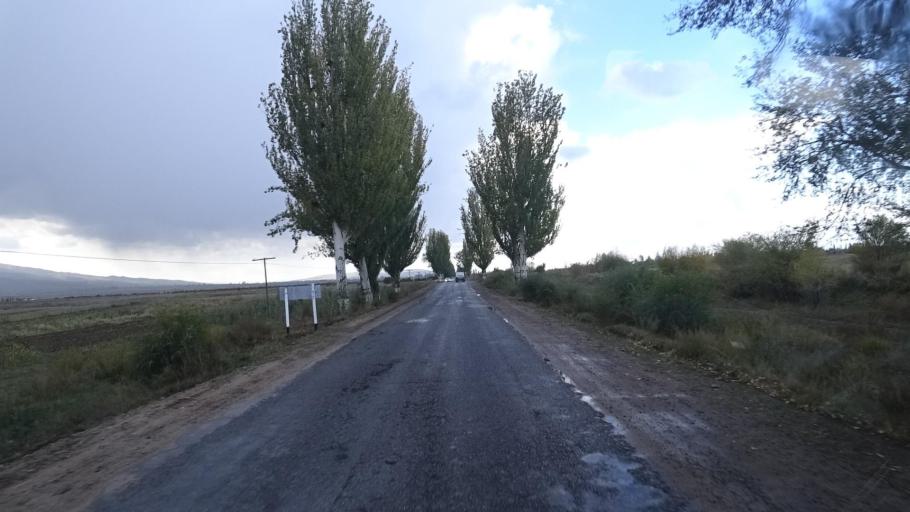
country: KG
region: Ysyk-Koel
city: Karakol
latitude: 42.4687
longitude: 78.2577
